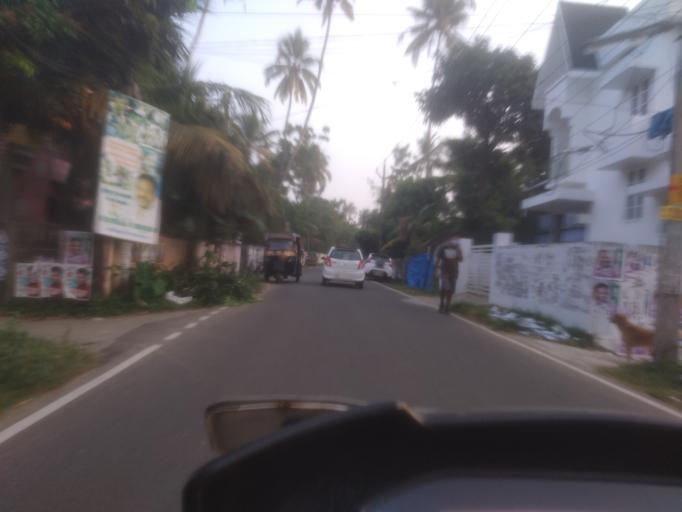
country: IN
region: Kerala
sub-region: Ernakulam
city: Cochin
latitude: 10.0068
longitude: 76.2196
